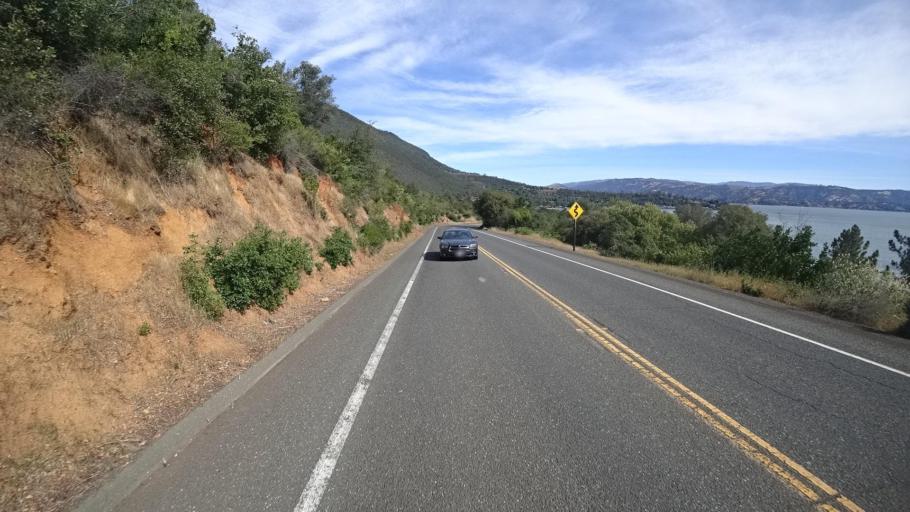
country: US
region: California
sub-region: Lake County
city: Soda Bay
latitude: 38.9647
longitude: -122.7368
